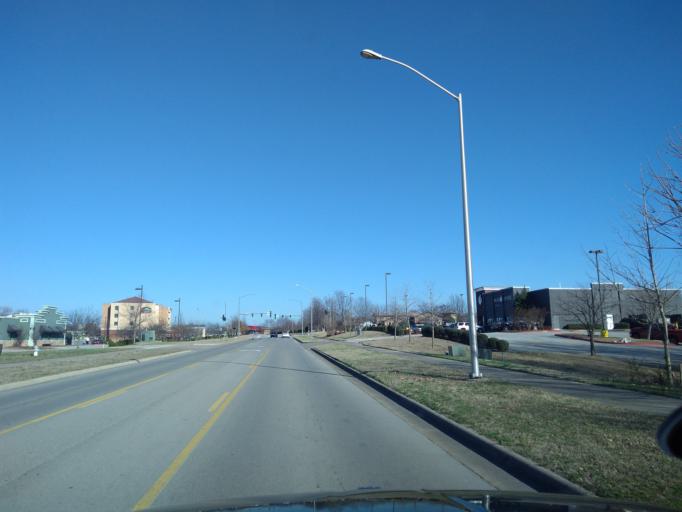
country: US
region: Arkansas
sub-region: Washington County
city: Johnson
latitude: 36.1176
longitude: -94.1520
